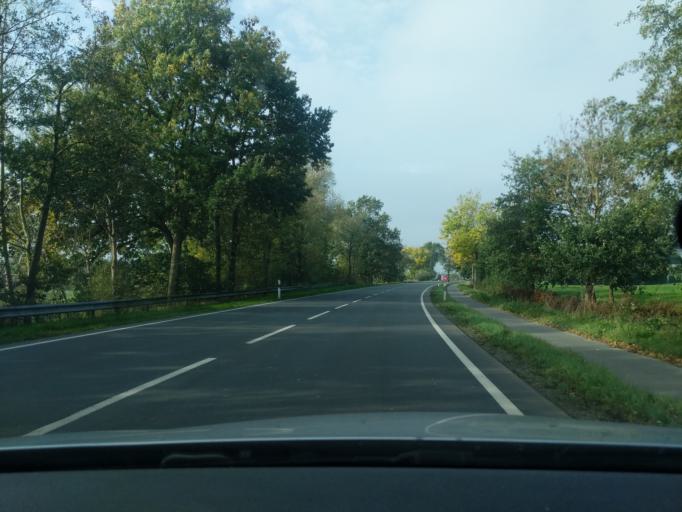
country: DE
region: Lower Saxony
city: Neuhaus an der Oste
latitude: 53.8011
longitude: 9.0275
